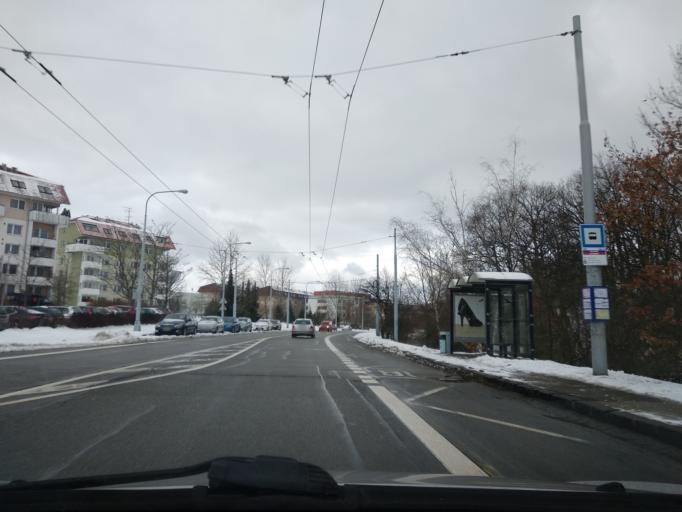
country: CZ
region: South Moravian
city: Troubsko
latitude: 49.1899
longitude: 16.5310
